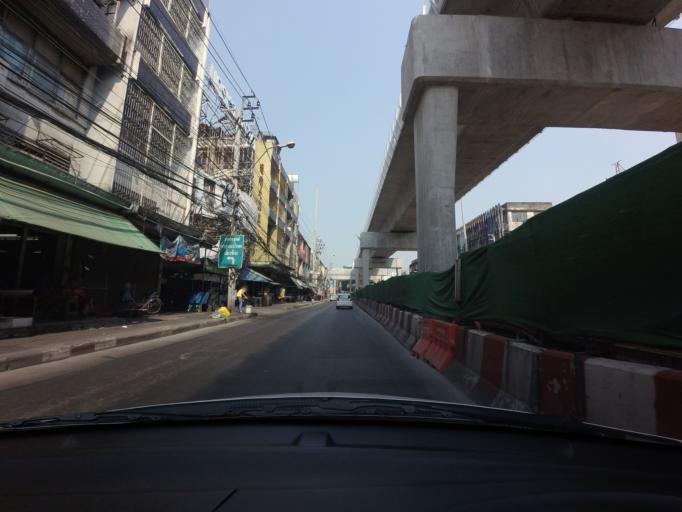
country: TH
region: Bangkok
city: Bangkok Noi
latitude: 13.7534
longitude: 100.4695
